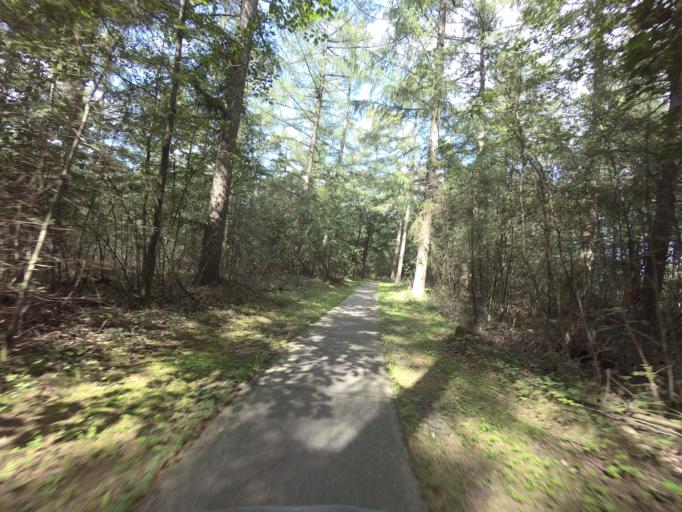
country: NL
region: Overijssel
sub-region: Gemeente Staphorst
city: Staphorst
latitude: 52.6216
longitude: 6.2718
